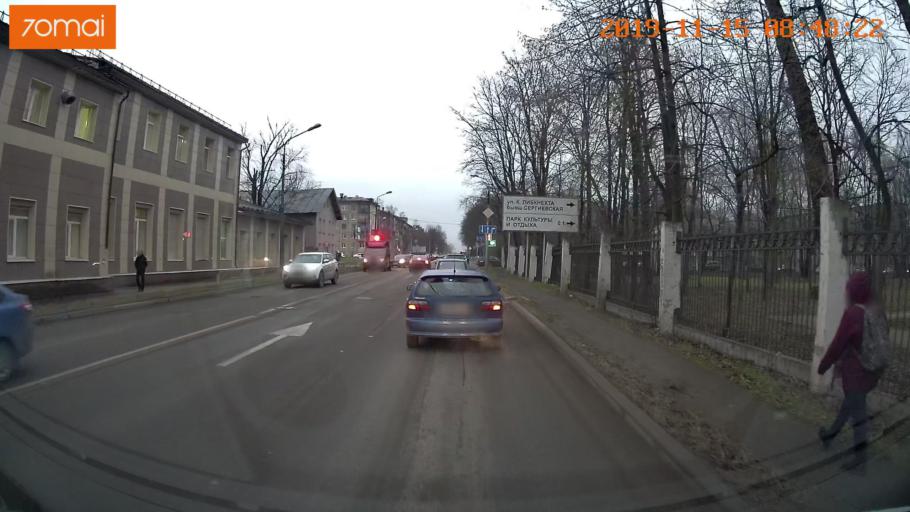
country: RU
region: Vologda
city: Cherepovets
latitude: 59.1217
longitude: 37.9183
